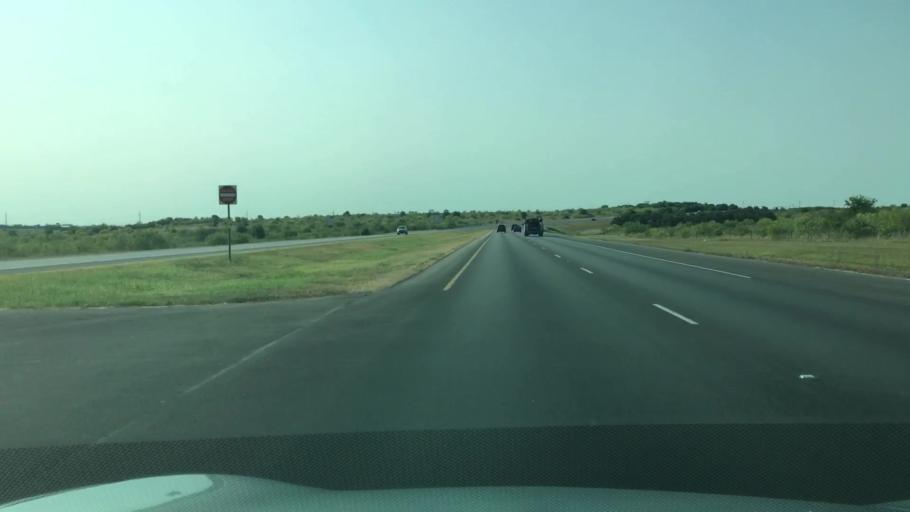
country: US
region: Texas
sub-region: Hays County
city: Kyle
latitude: 30.0412
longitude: -97.8738
